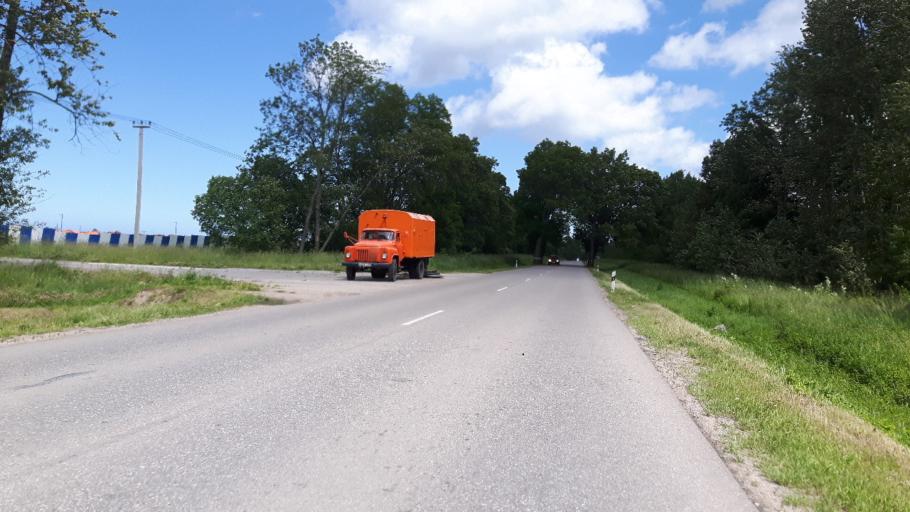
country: RU
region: Kaliningrad
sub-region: Zelenogradskiy Rayon
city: Zelenogradsk
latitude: 54.9343
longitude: 20.4381
